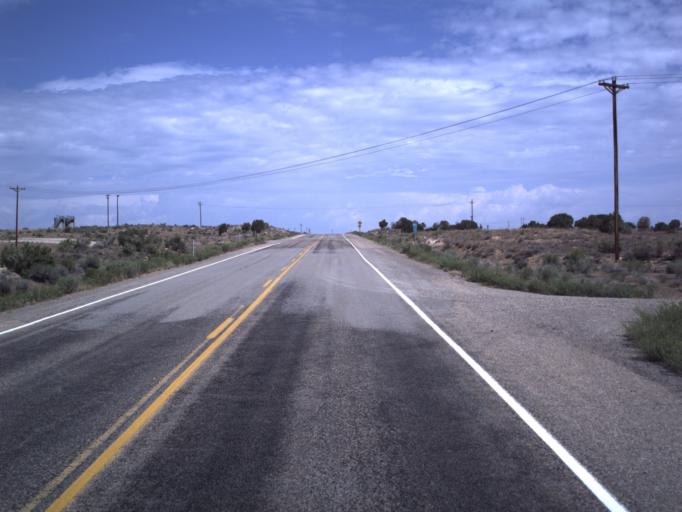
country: US
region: Utah
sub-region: Uintah County
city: Naples
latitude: 40.1760
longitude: -109.3223
